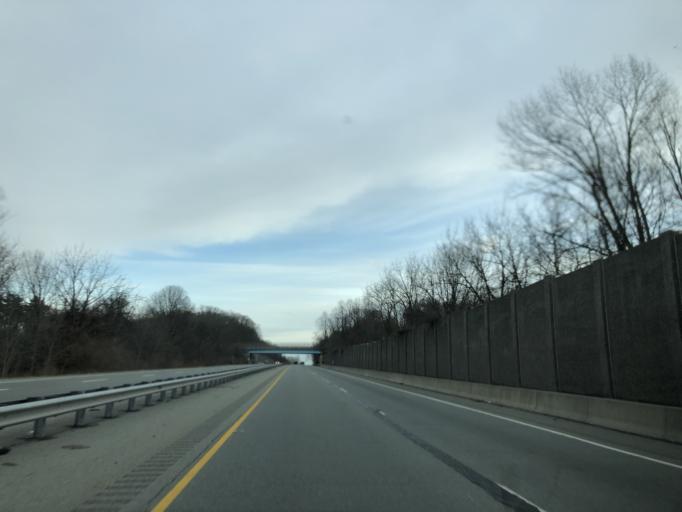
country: US
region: Pennsylvania
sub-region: Chester County
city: Exton
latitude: 40.0056
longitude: -75.6071
